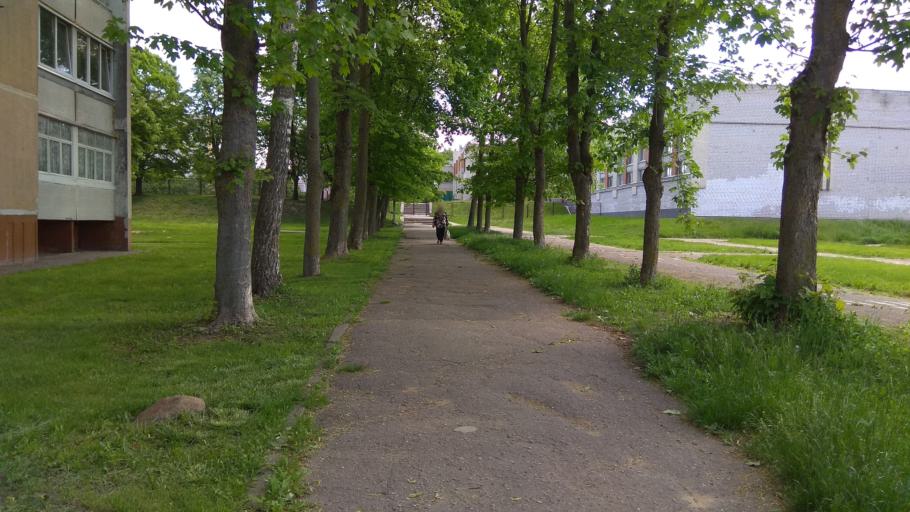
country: BY
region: Grodnenskaya
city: Hrodna
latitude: 53.7076
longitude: 23.7986
